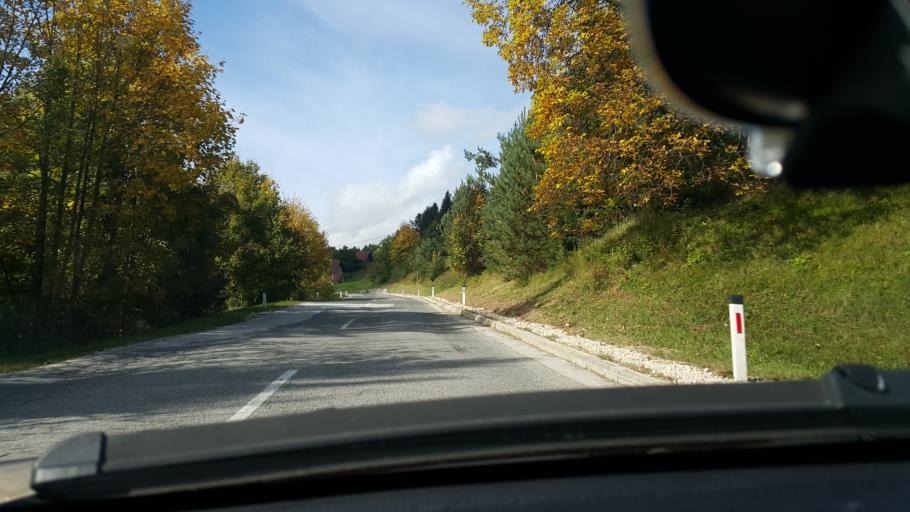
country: SI
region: Zrece
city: Zrece
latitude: 46.3746
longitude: 15.3384
